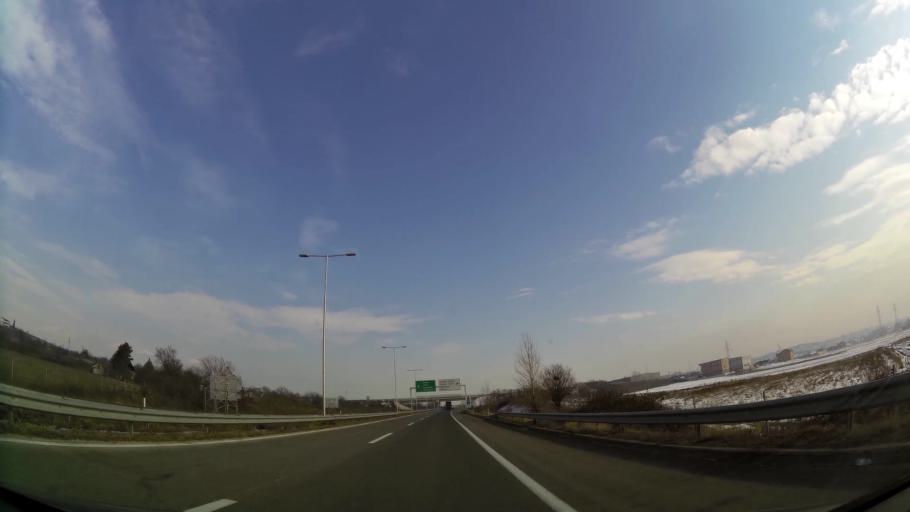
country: MK
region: Suto Orizari
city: Suto Orizare
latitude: 42.0531
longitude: 21.4151
